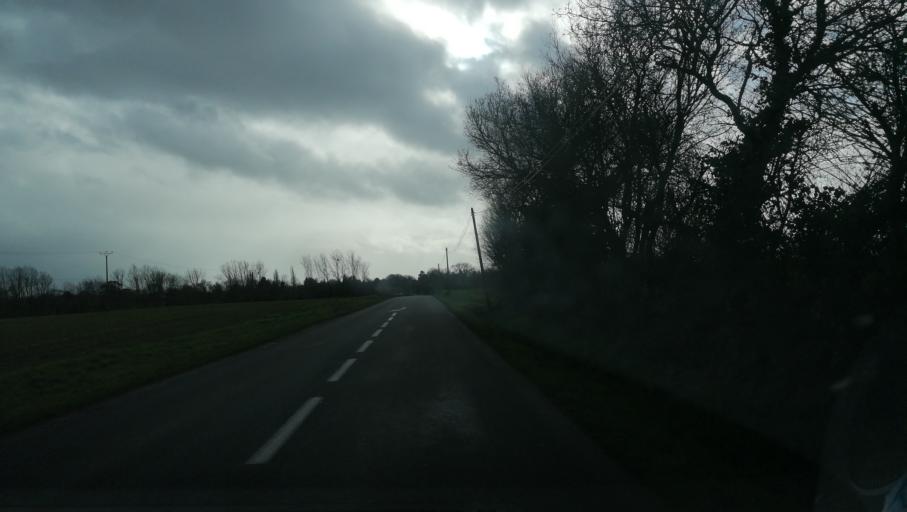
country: FR
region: Brittany
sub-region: Departement des Cotes-d'Armor
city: Lantic
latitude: 48.5865
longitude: -2.9157
